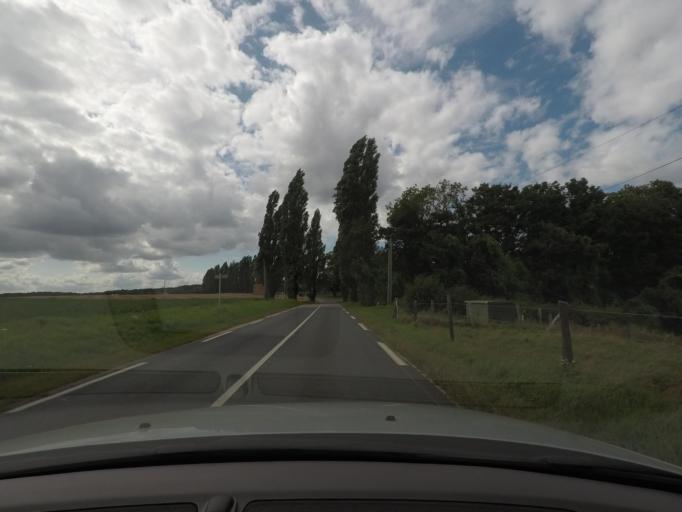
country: FR
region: Haute-Normandie
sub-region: Departement de l'Eure
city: Les Andelys
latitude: 49.2371
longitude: 1.4253
